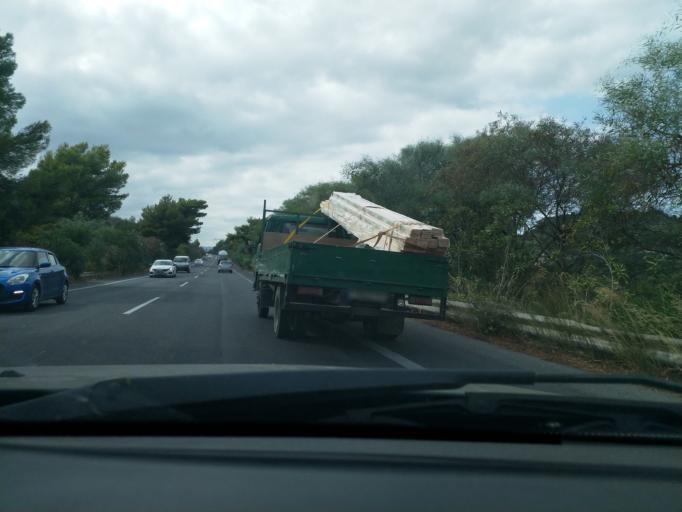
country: GR
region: Crete
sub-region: Nomos Chanias
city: Georgioupolis
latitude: 35.3647
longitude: 24.2360
